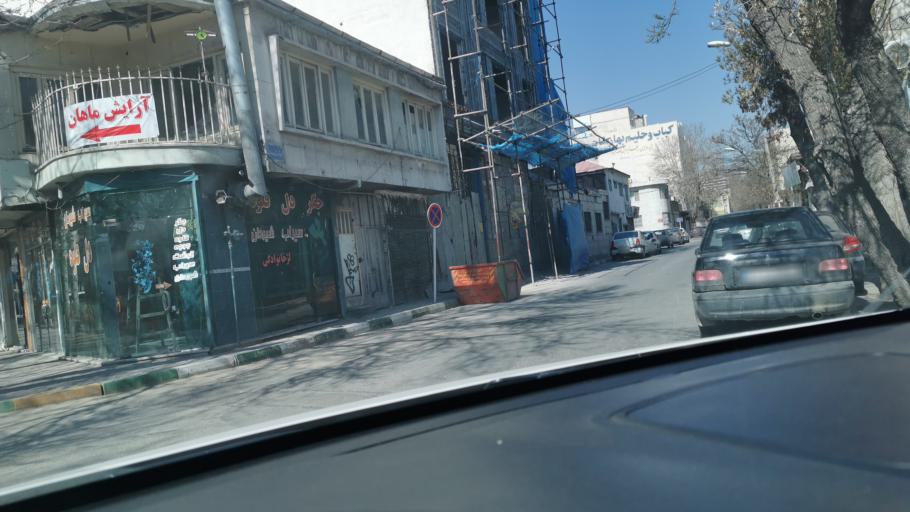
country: IR
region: Razavi Khorasan
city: Mashhad
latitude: 36.2836
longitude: 59.5919
